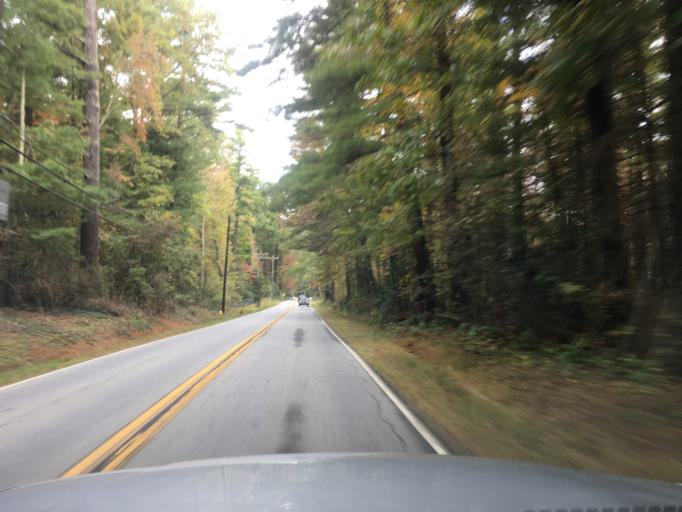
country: US
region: North Carolina
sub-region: Henderson County
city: Flat Rock
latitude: 35.2608
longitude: -82.4386
